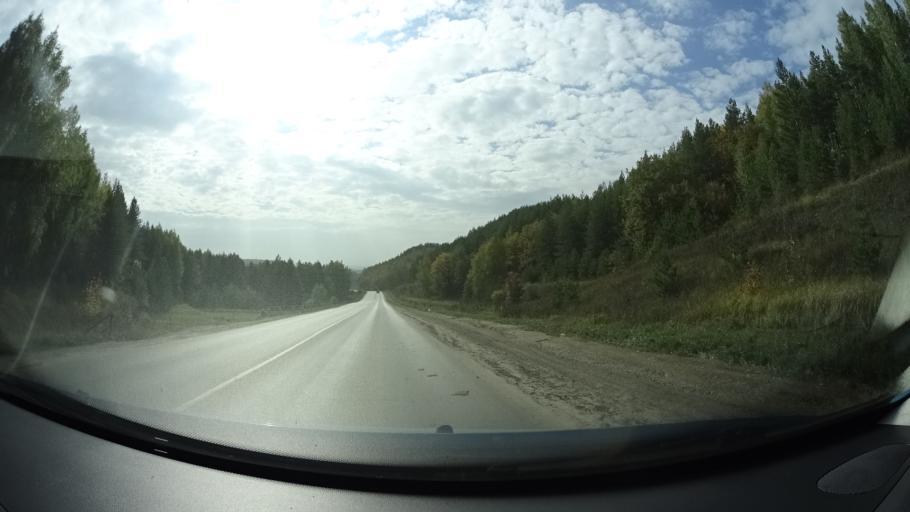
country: RU
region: Bashkortostan
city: Oktyabr'skiy
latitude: 54.5393
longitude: 53.5640
